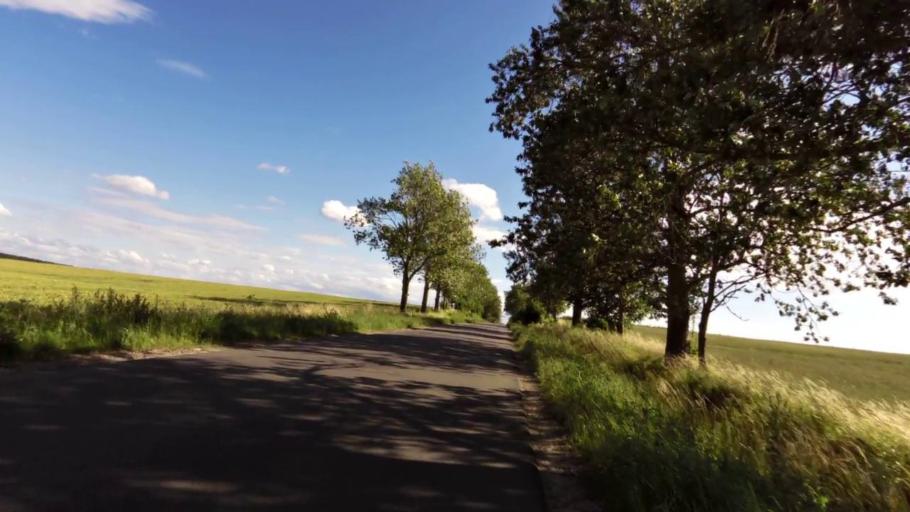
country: PL
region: West Pomeranian Voivodeship
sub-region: Powiat slawienski
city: Slawno
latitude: 54.4446
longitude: 16.7354
